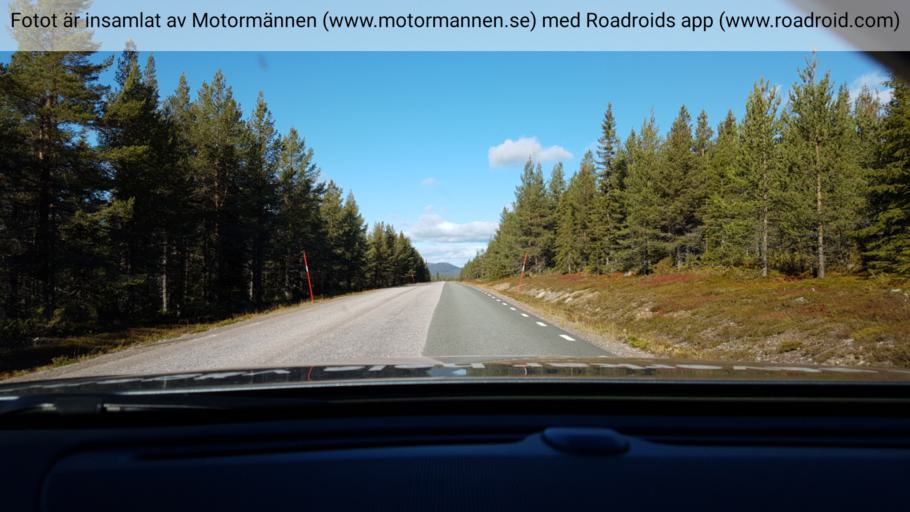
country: SE
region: Norrbotten
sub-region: Arjeplogs Kommun
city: Arjeplog
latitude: 65.8103
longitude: 18.4563
